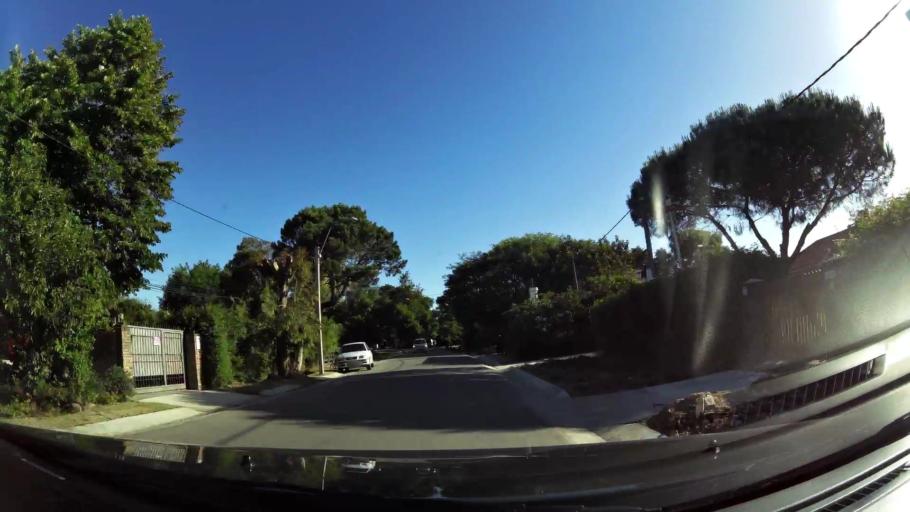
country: UY
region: Canelones
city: Barra de Carrasco
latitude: -34.8645
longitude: -56.0341
